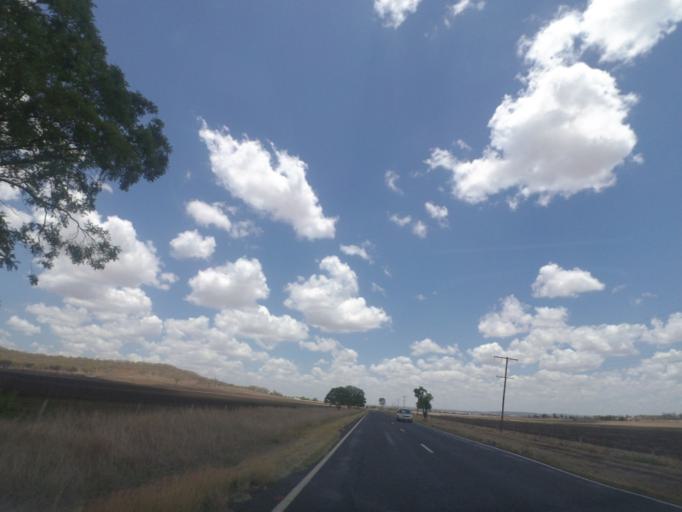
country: AU
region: Queensland
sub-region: Southern Downs
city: Warwick
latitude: -28.0099
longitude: 151.9890
